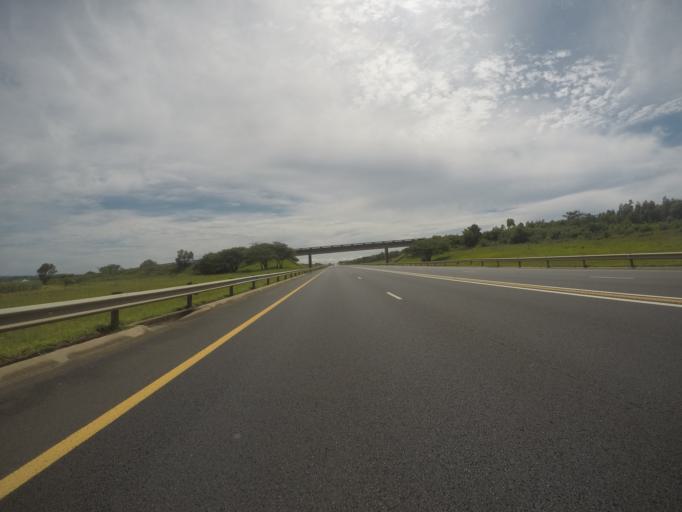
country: ZA
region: KwaZulu-Natal
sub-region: iLembe District Municipality
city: Mandeni
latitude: -29.1546
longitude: 31.5399
